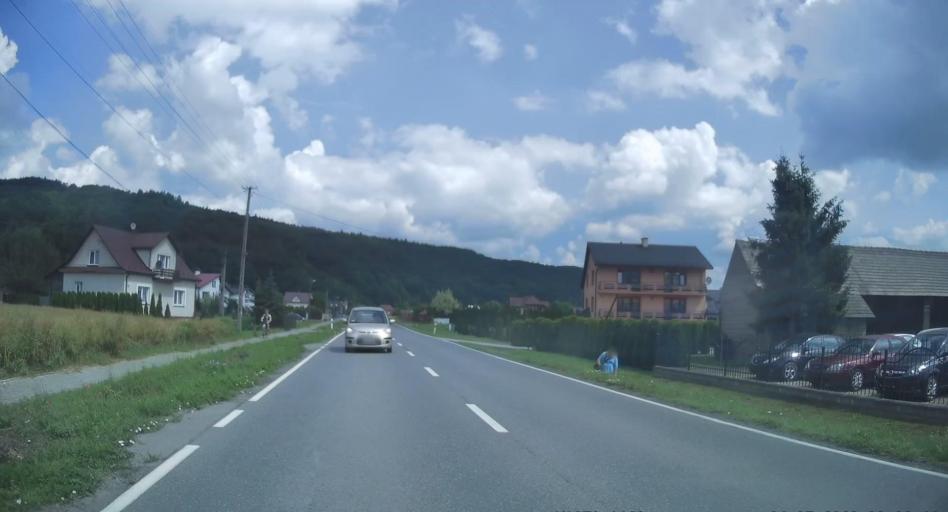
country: PL
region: Lesser Poland Voivodeship
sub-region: Powiat tarnowski
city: Wielka Wies
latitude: 49.9132
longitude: 20.8207
